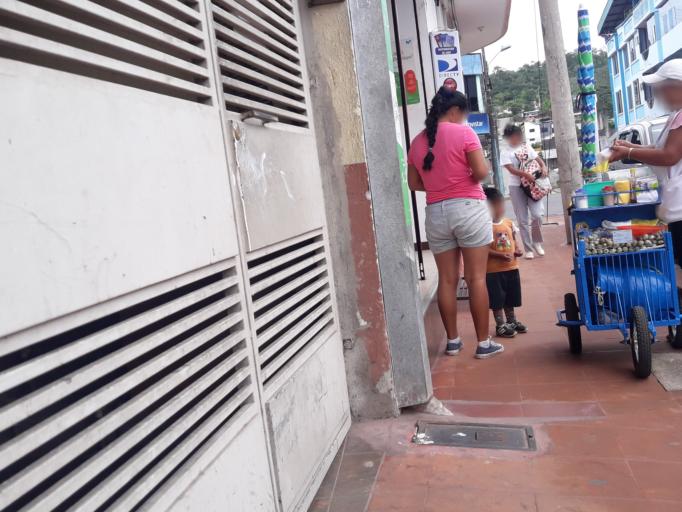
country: EC
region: Napo
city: Tena
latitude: -1.0012
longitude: -77.8118
